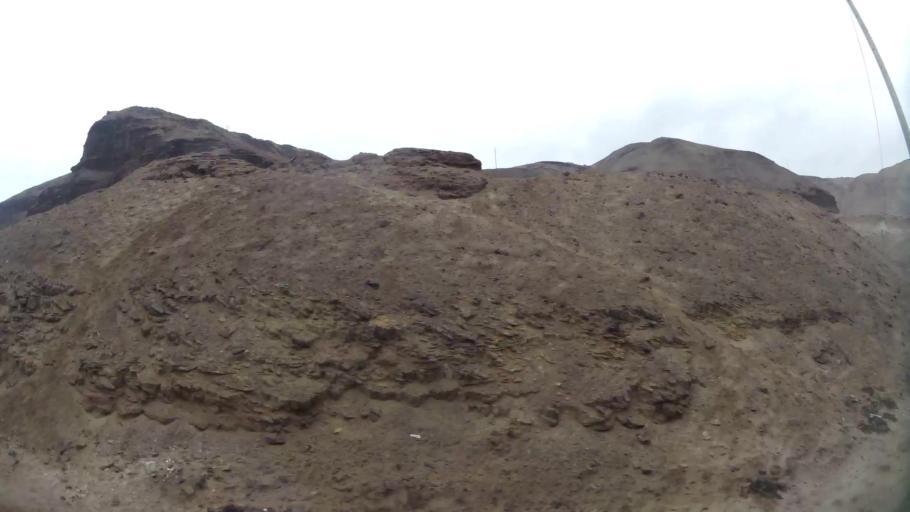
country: PE
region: Lima
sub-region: Lima
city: Surco
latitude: -12.1707
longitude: -77.0357
